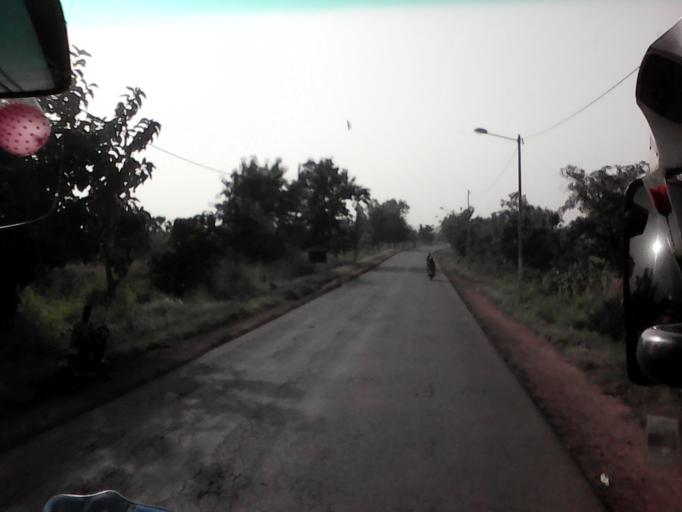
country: TG
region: Kara
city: Kara
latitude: 9.5259
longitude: 1.2060
